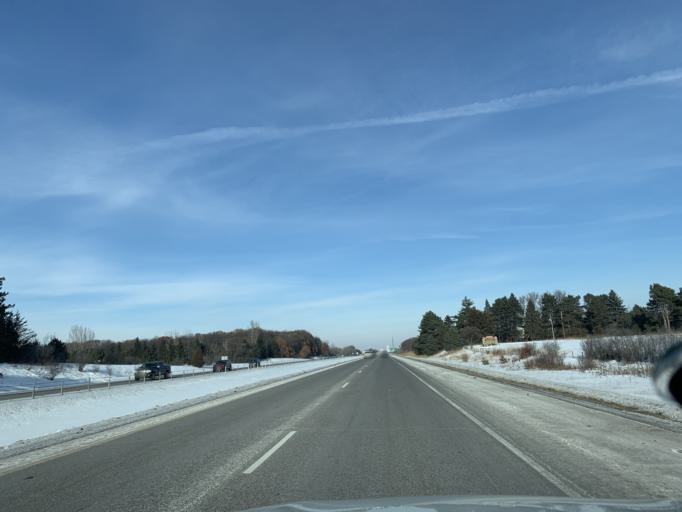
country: US
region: Minnesota
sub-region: Chisago County
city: Wyoming
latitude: 45.3134
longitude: -93.0033
